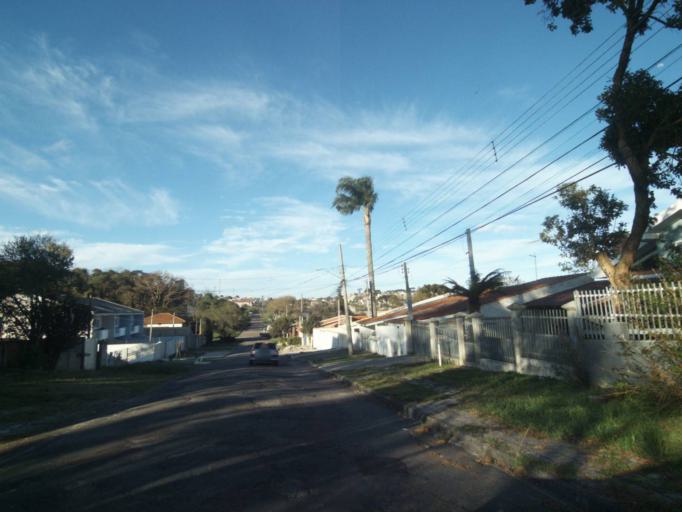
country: BR
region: Parana
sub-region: Curitiba
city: Curitiba
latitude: -25.3805
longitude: -49.2515
